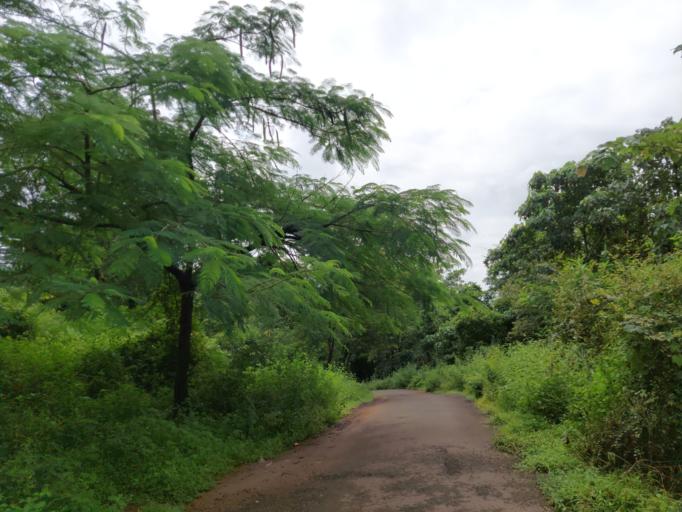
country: IN
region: Maharashtra
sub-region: Ratnagiri
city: Chiplun
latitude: 17.5581
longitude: 73.5071
